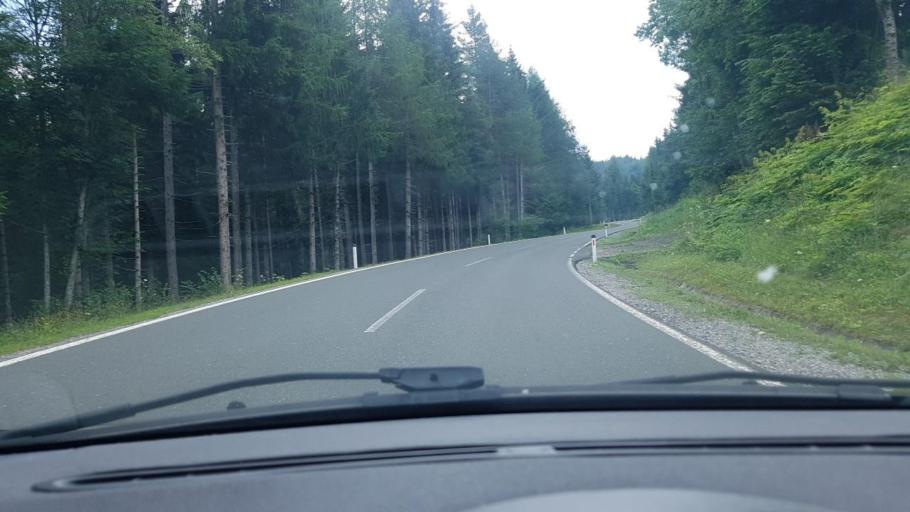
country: AT
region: Carinthia
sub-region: Politischer Bezirk Spittal an der Drau
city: Steinfeld
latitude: 46.7305
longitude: 13.2301
